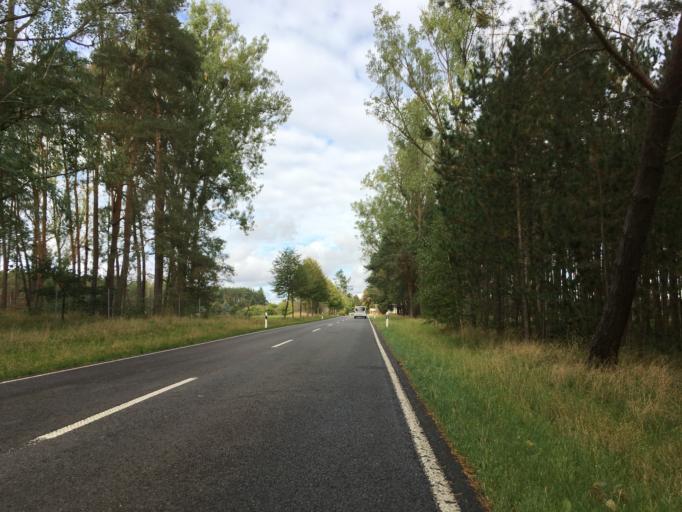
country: PL
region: West Pomeranian Voivodeship
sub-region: Powiat gryfinski
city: Cedynia
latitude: 52.9100
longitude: 14.1207
